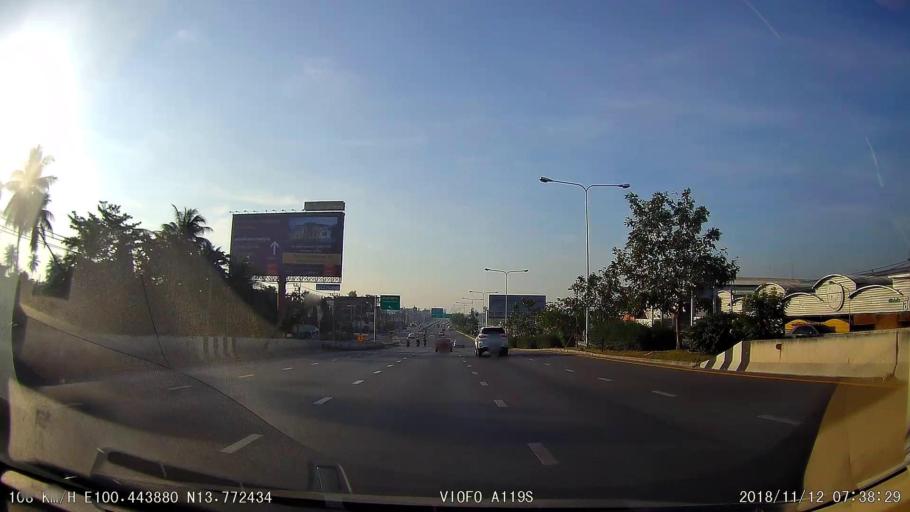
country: TH
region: Bangkok
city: Taling Chan
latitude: 13.7712
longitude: 100.4440
